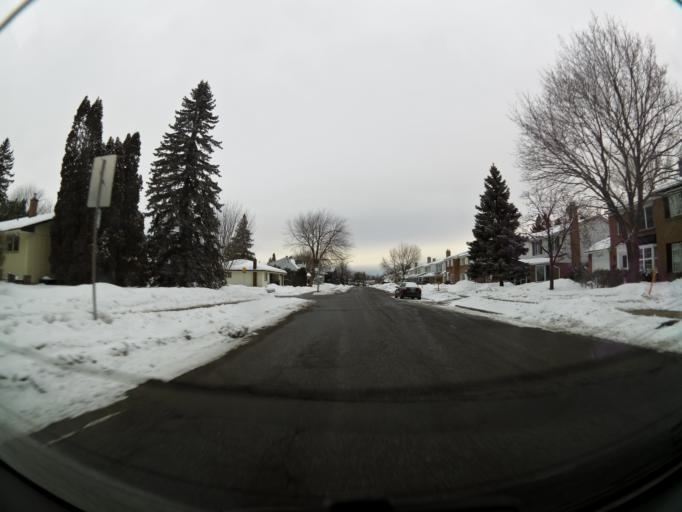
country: CA
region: Quebec
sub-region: Outaouais
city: Gatineau
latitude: 45.4536
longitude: -75.5937
